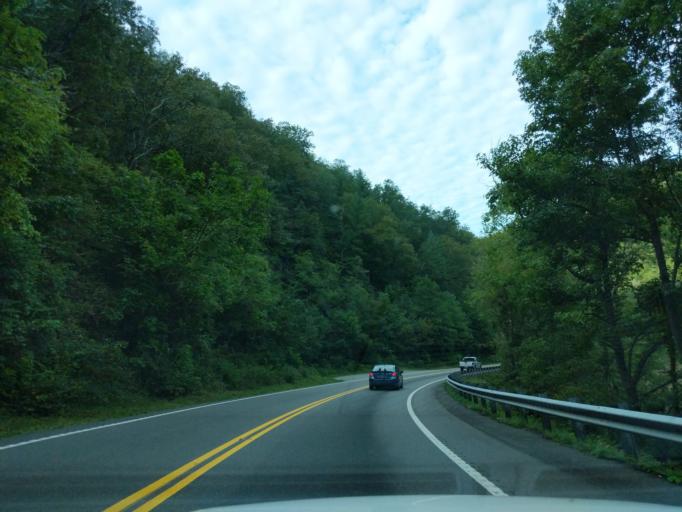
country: US
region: Georgia
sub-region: Fannin County
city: McCaysville
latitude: 35.0785
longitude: -84.5062
